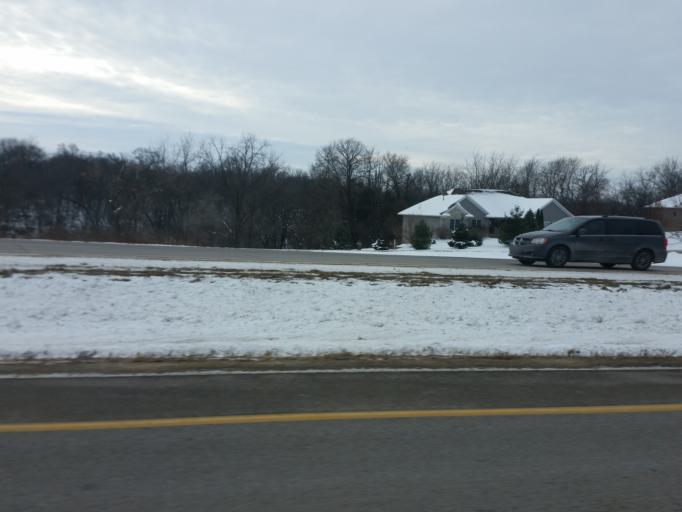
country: US
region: Iowa
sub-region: Dubuque County
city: Dyersville
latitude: 42.4689
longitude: -91.0852
